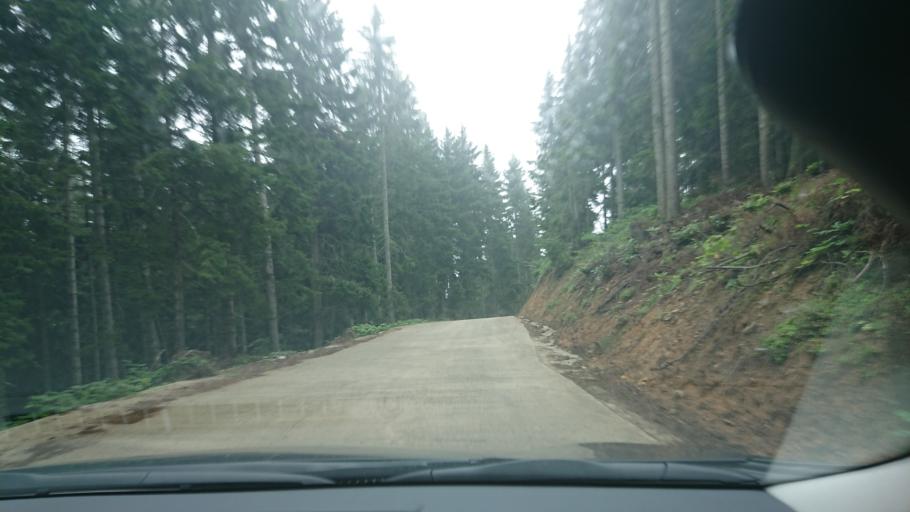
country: TR
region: Gumushane
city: Kurtun
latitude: 40.6647
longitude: 39.0152
